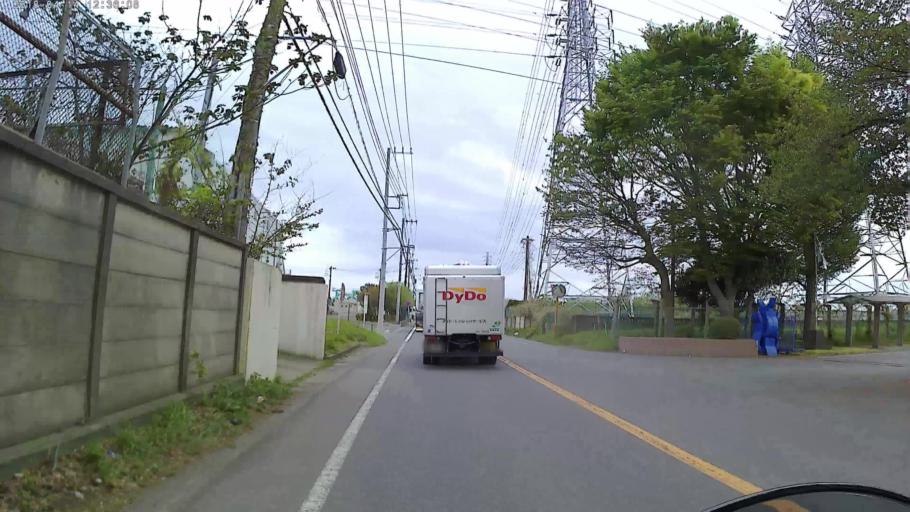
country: JP
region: Kanagawa
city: Atsugi
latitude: 35.4174
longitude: 139.4079
